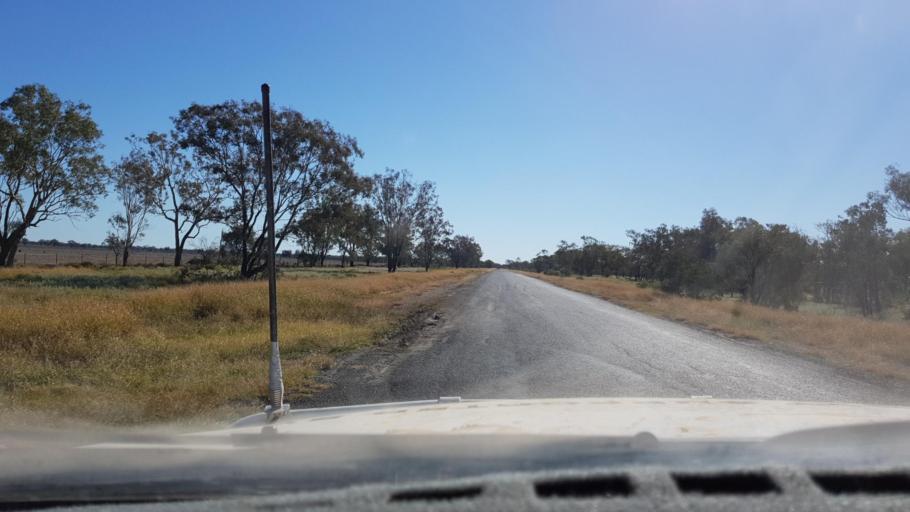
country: AU
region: New South Wales
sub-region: Walgett
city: Lightning Ridge
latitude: -29.5772
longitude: 148.6777
